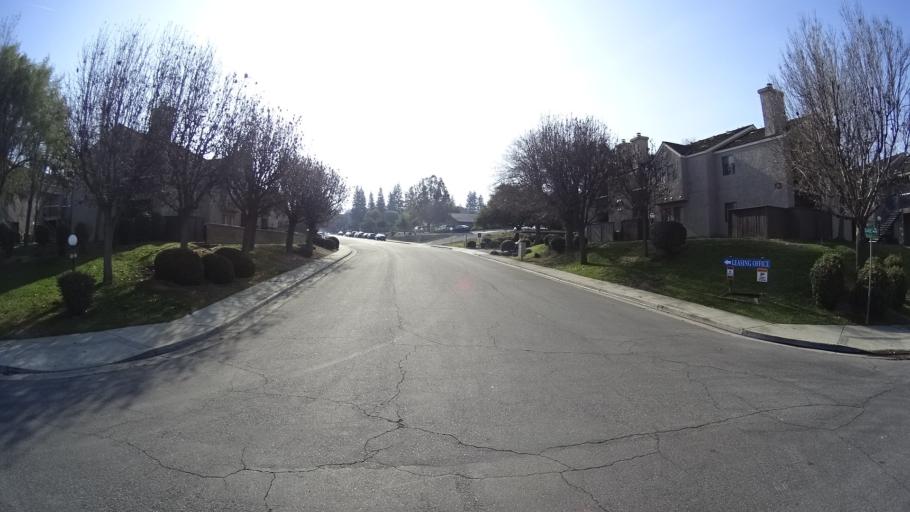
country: US
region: California
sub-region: Kern County
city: Oildale
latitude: 35.4115
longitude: -118.9360
